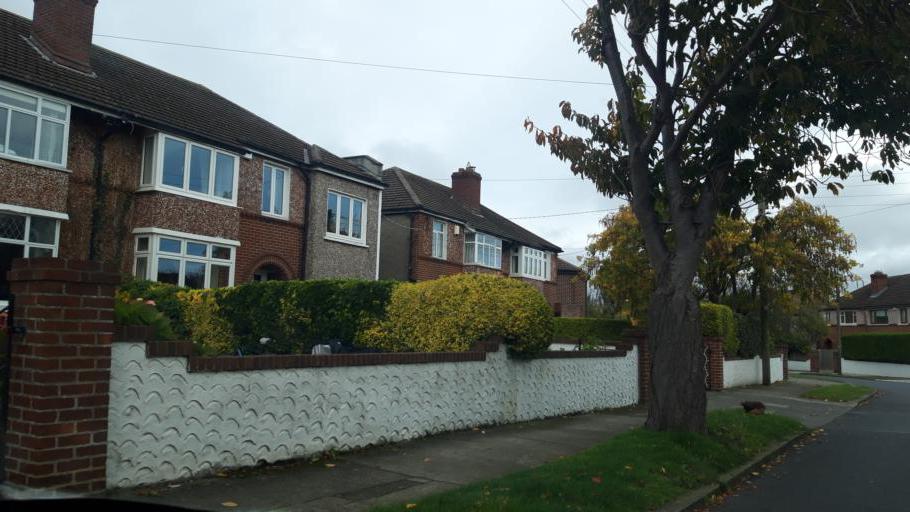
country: IE
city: Milltown
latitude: 53.3077
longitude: -6.2400
